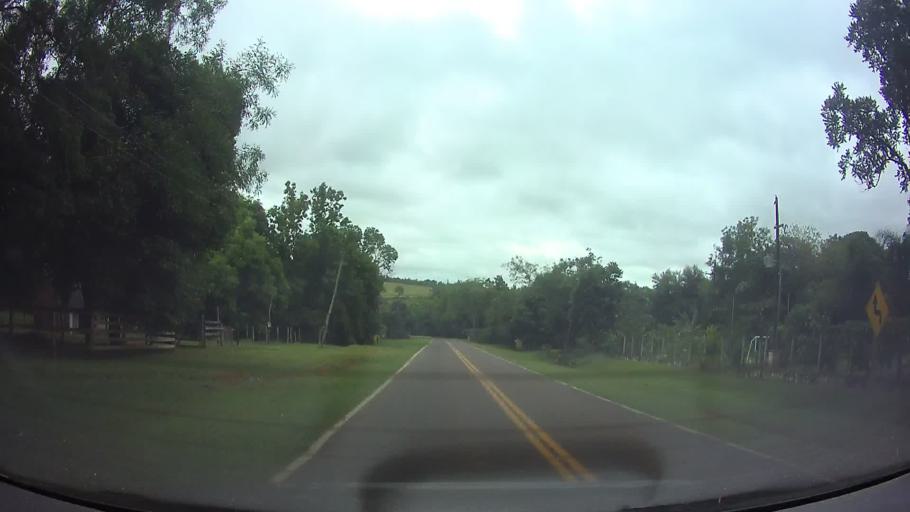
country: PY
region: Paraguari
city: Acahay
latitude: -25.9313
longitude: -57.1057
